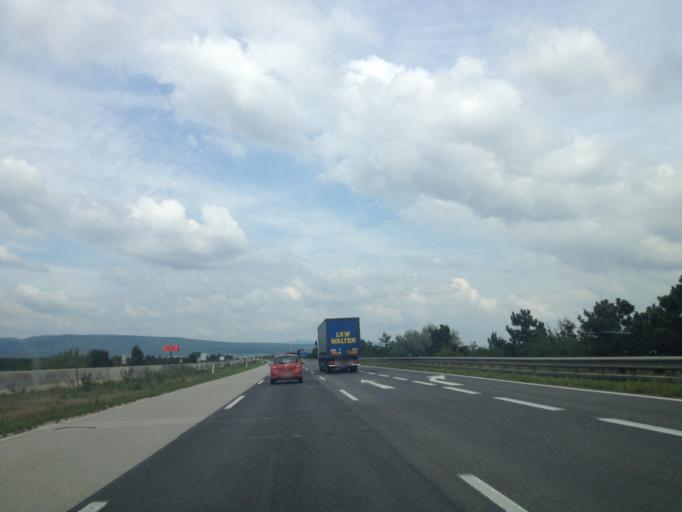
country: AT
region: Lower Austria
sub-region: Wiener Neustadt Stadt
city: Wiener Neustadt
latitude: 47.7993
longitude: 16.2021
